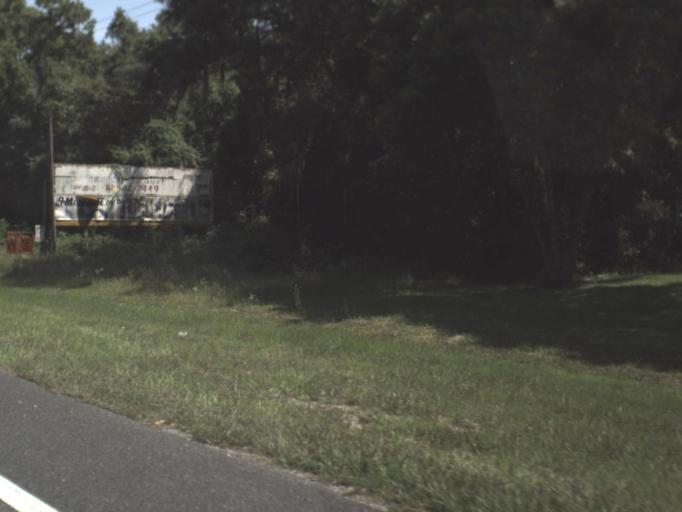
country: US
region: Florida
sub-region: Levy County
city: Manatee Road
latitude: 29.5628
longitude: -82.9076
